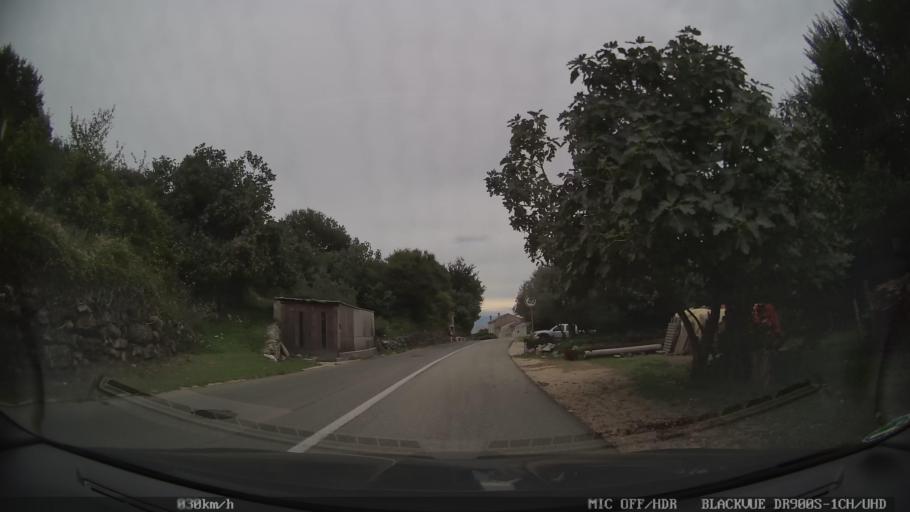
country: HR
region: Primorsko-Goranska
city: Punat
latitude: 45.0000
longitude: 14.7091
